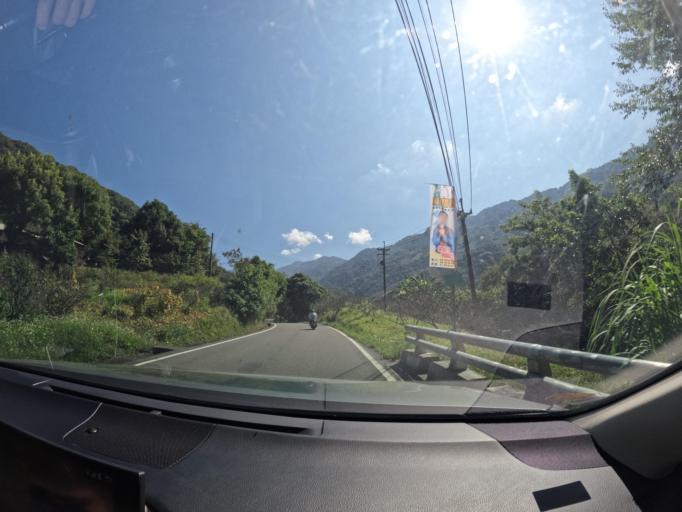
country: TW
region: Taiwan
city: Yujing
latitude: 23.1426
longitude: 120.7444
